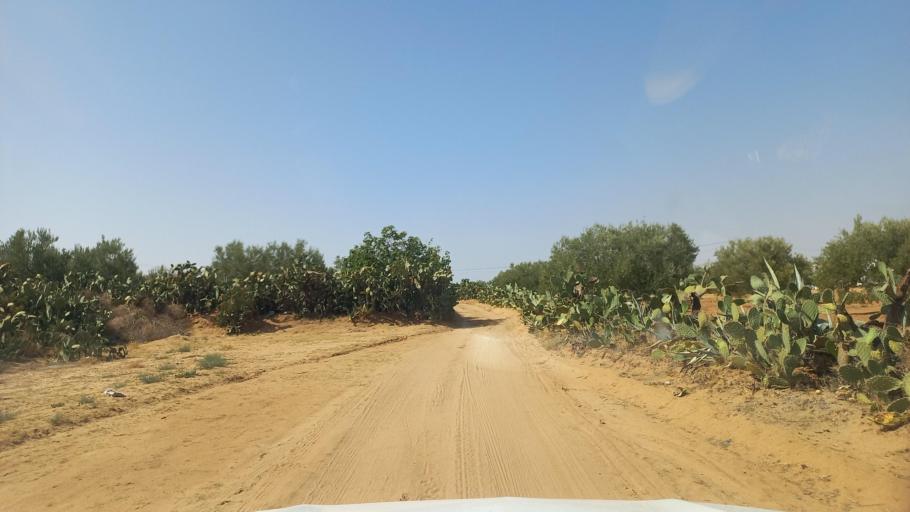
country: TN
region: Al Qasrayn
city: Kasserine
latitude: 35.2377
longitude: 9.0455
